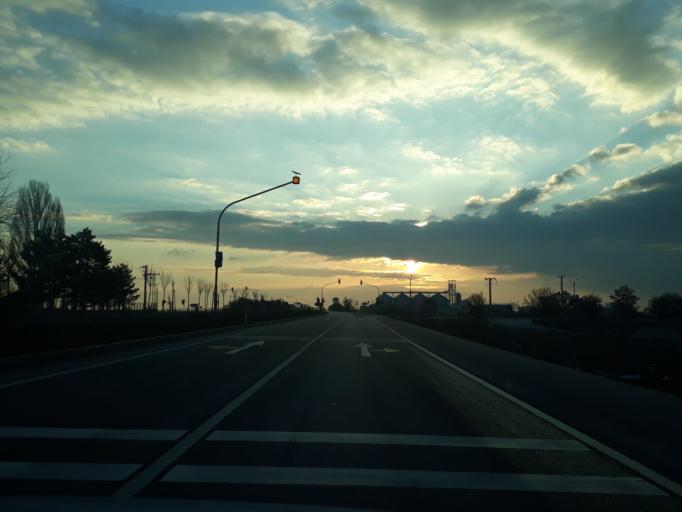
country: TR
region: Konya
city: Ovakavagi
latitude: 37.7382
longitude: 33.0430
